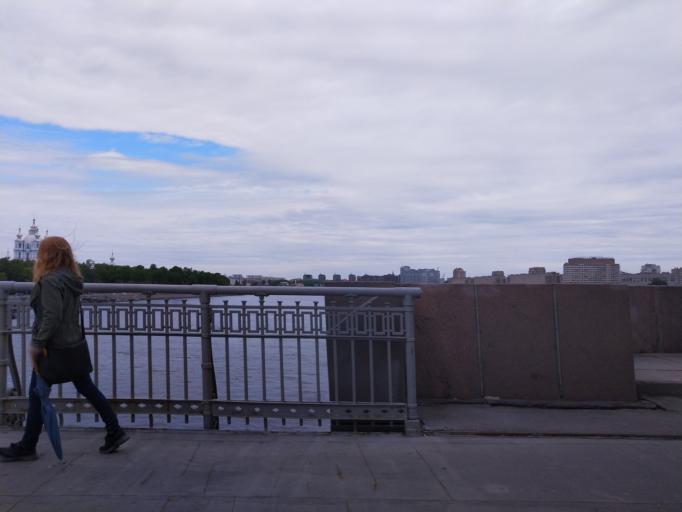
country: RU
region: St.-Petersburg
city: Centralniy
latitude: 59.9427
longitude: 30.4018
